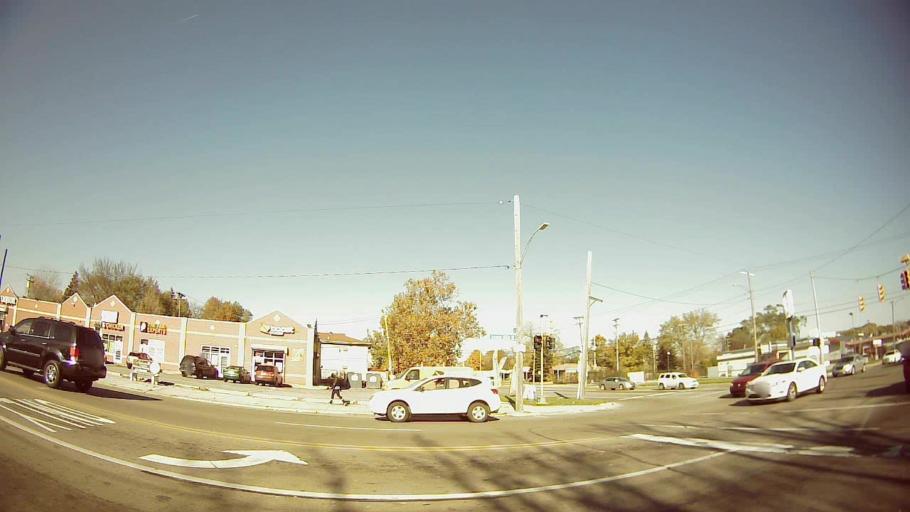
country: US
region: Michigan
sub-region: Wayne County
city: Redford
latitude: 42.4290
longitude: -83.2614
